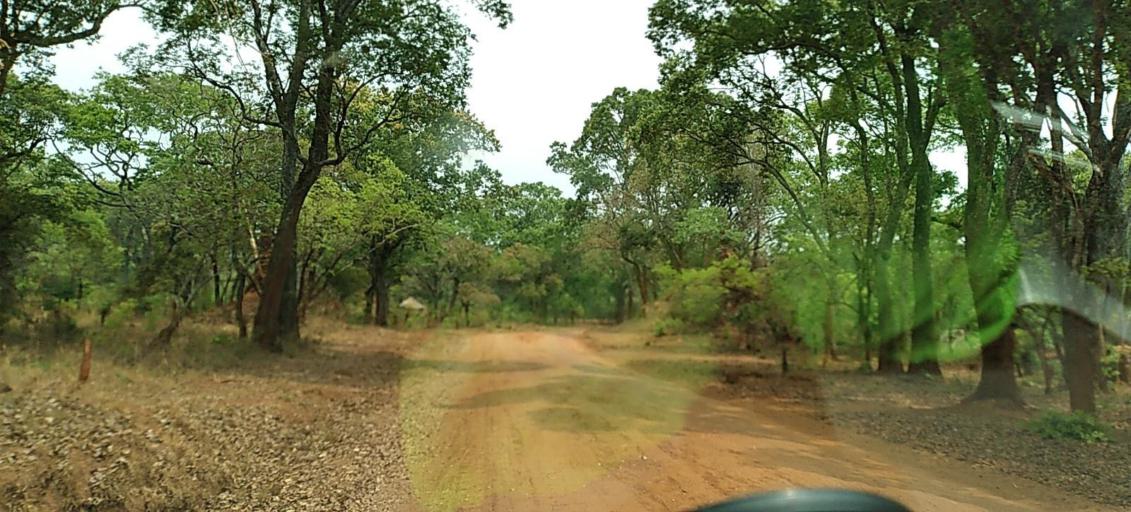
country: ZM
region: North-Western
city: Solwezi
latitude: -12.8063
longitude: 26.5384
